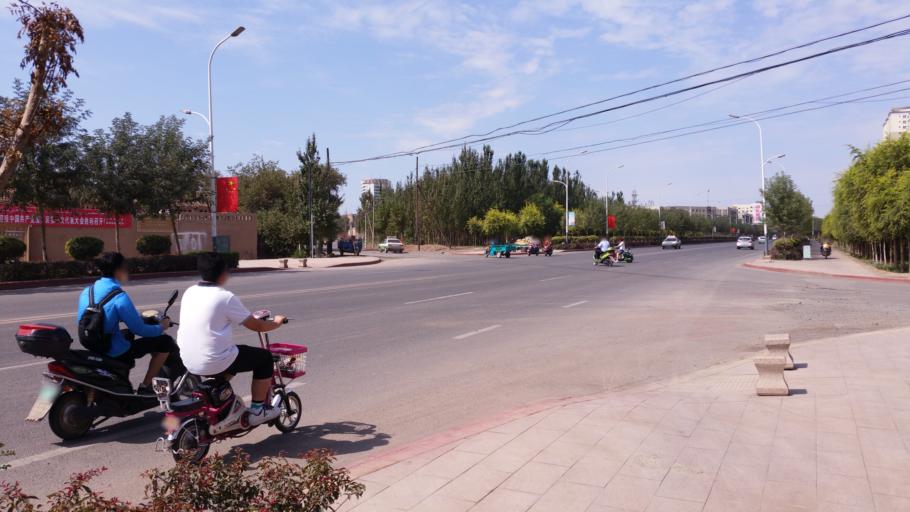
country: CN
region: Xinjiang Uygur Zizhiqu
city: Laochenglu
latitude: 42.9504
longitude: 89.1984
